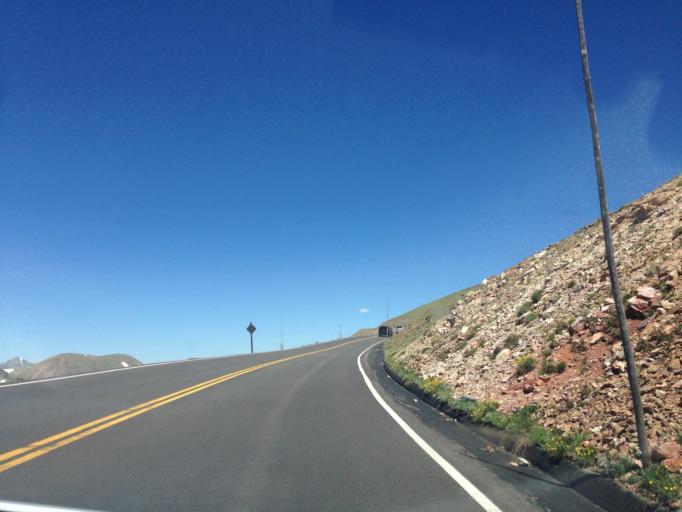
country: US
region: Colorado
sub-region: Larimer County
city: Estes Park
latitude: 40.4251
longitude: -105.7564
